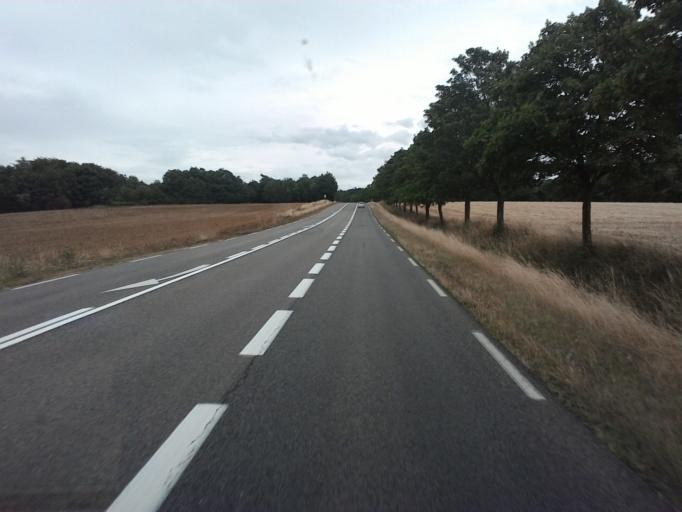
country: FR
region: Lorraine
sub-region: Departement de Meurthe-et-Moselle
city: Colombey-les-Belles
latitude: 48.5758
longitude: 5.9840
